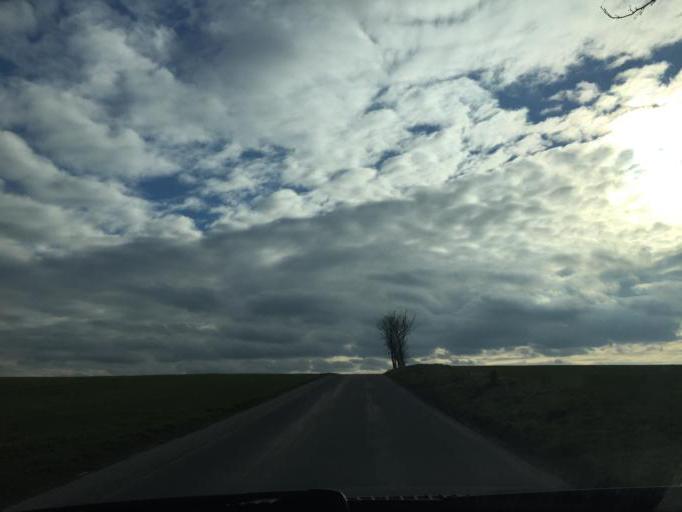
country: DE
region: Saxony
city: Ebersbach
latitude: 51.2233
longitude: 13.6629
